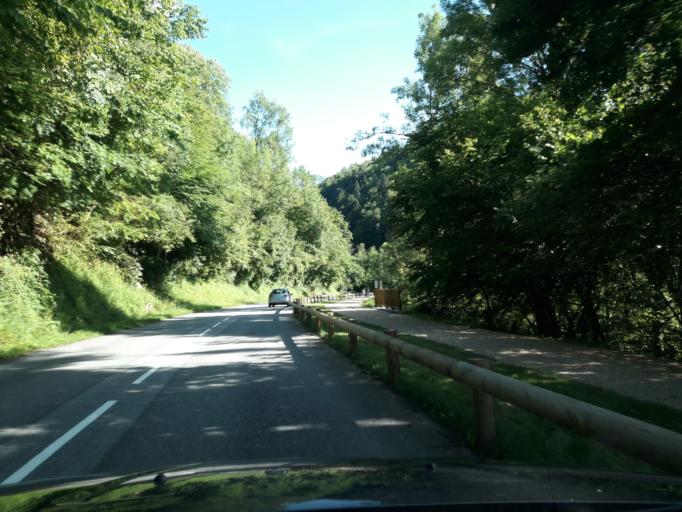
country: FR
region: Rhone-Alpes
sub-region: Departement de la Savoie
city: Vimines
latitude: 45.5612
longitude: 5.8125
